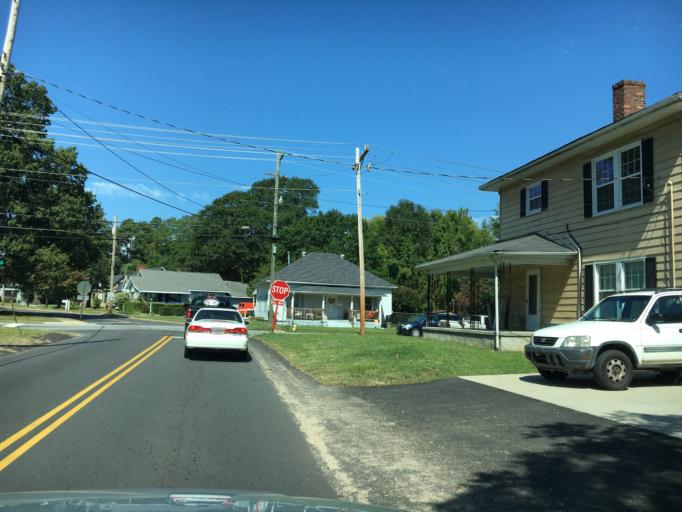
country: US
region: South Carolina
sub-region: Greenville County
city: Greer
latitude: 34.9319
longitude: -82.2265
